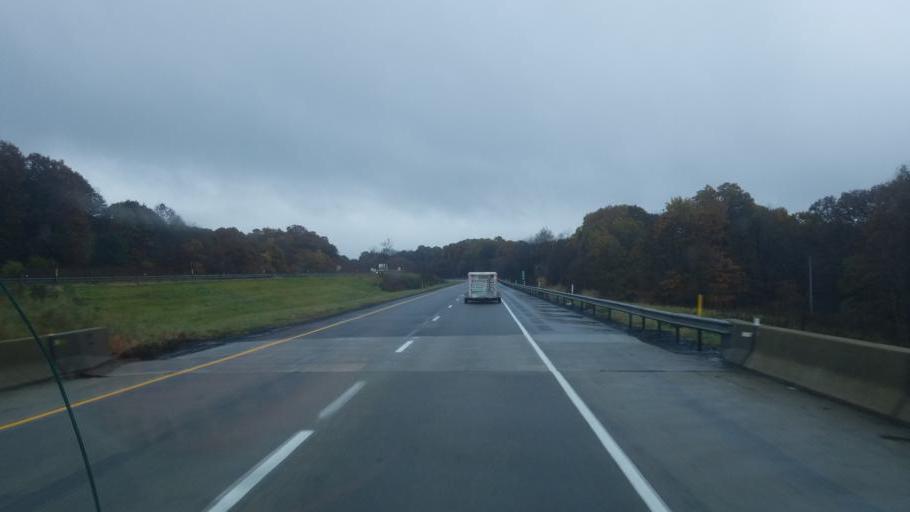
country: US
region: Pennsylvania
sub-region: Clarion County
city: Knox
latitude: 41.1903
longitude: -79.6118
